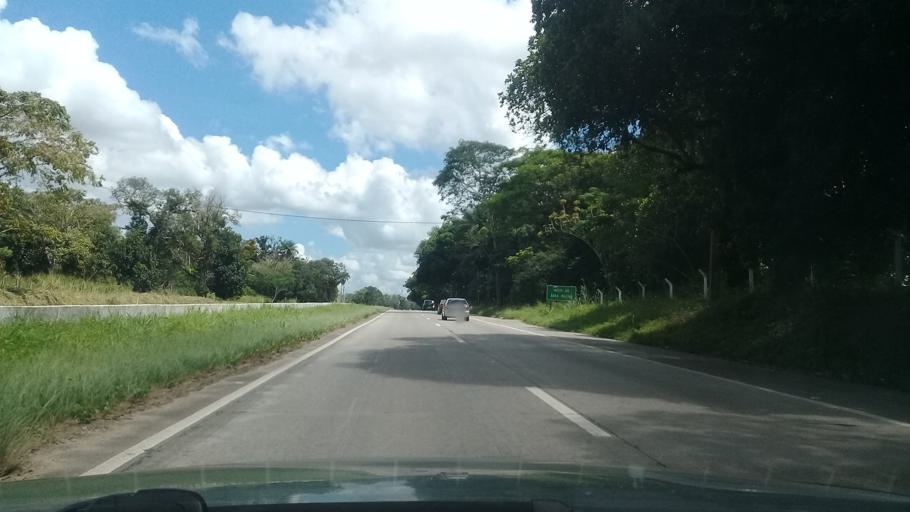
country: BR
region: Pernambuco
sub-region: Carpina
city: Carpina
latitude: -7.9257
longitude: -35.1504
